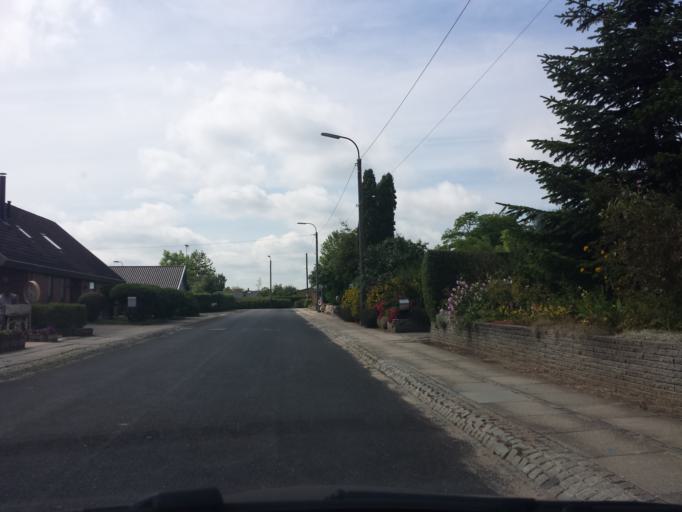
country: DK
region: Capital Region
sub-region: Ballerup Kommune
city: Ballerup
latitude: 55.7110
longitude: 12.3960
